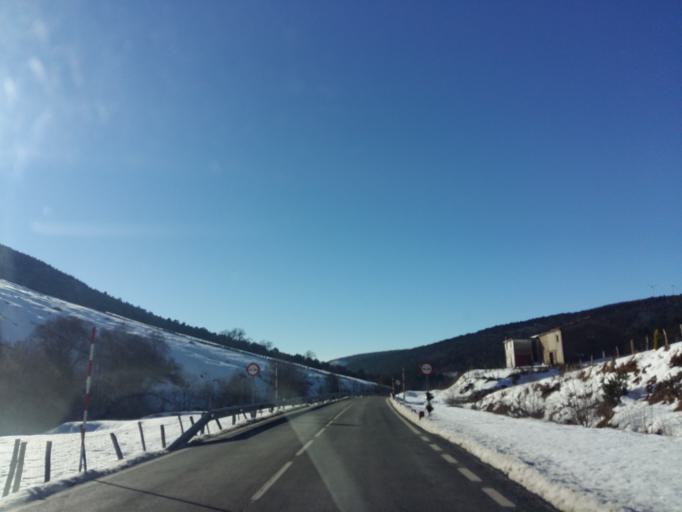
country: ES
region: Basque Country
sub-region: Bizkaia
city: Lanestosa
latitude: 43.1366
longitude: -3.4533
